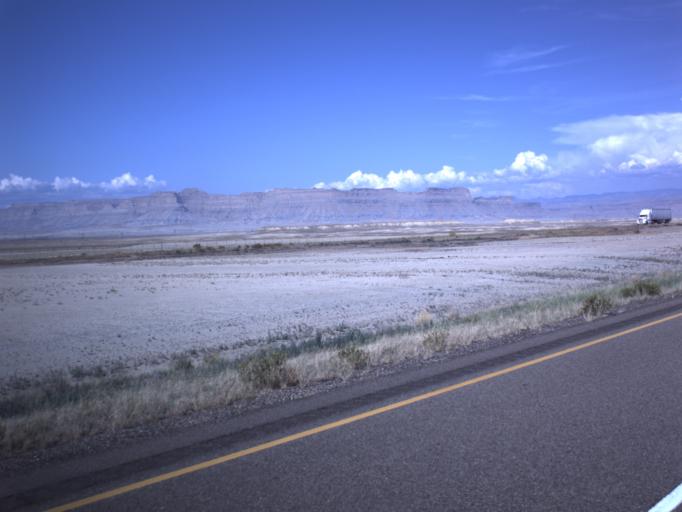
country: US
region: Utah
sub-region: Carbon County
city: East Carbon City
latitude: 38.9547
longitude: -110.3050
